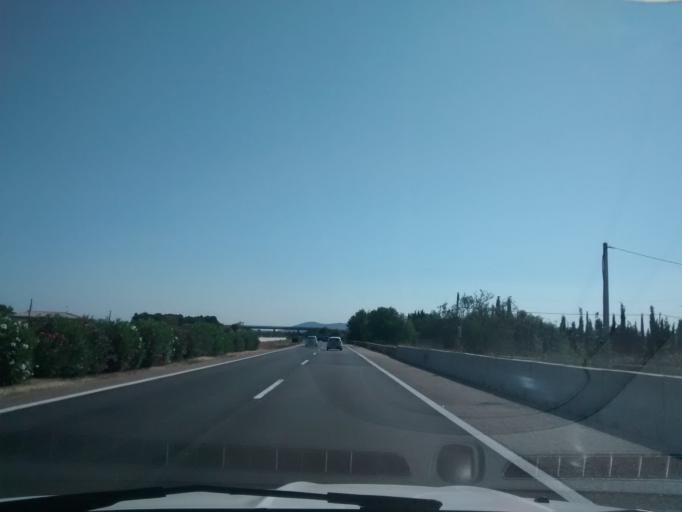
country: ES
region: Balearic Islands
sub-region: Illes Balears
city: Binissalem
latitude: 39.6814
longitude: 2.8522
